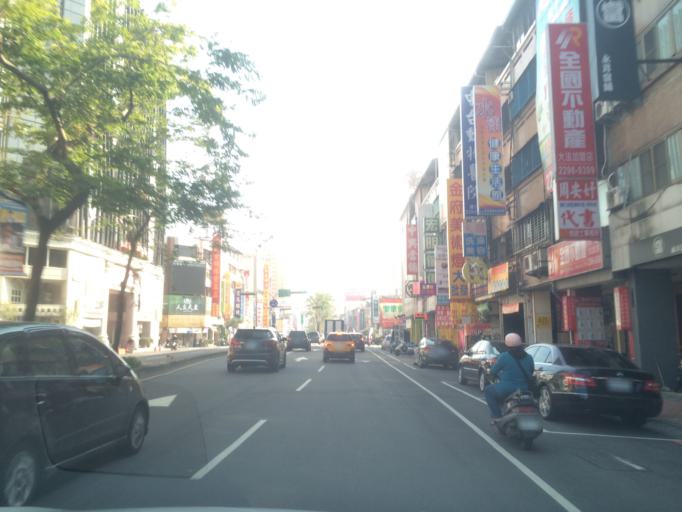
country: TW
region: Taiwan
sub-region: Taichung City
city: Taichung
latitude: 24.1725
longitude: 120.6716
